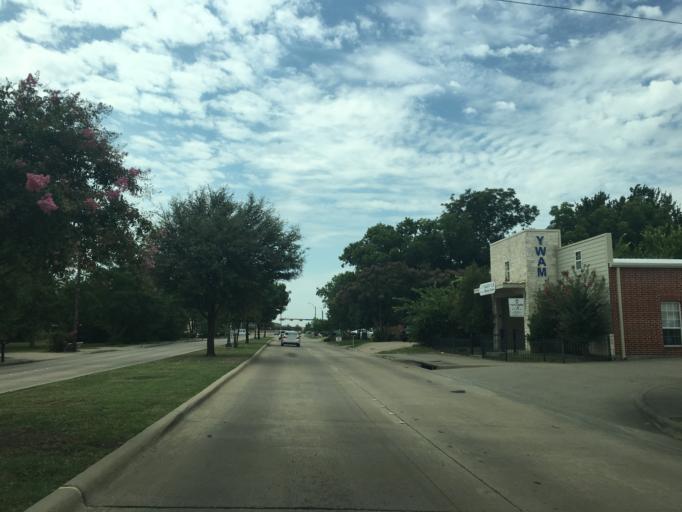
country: US
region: Texas
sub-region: Collin County
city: Wylie
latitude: 33.0082
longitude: -96.5391
